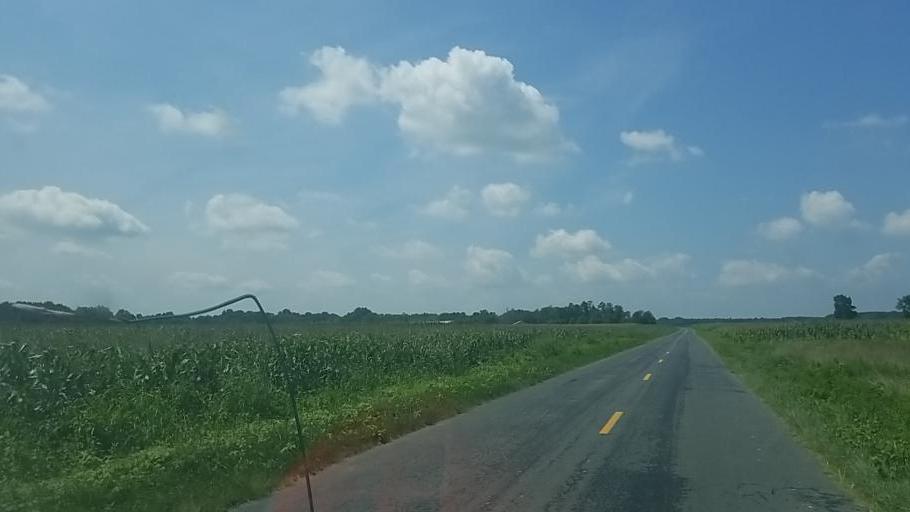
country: US
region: Maryland
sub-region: Talbot County
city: Easton
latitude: 38.7821
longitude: -76.0019
